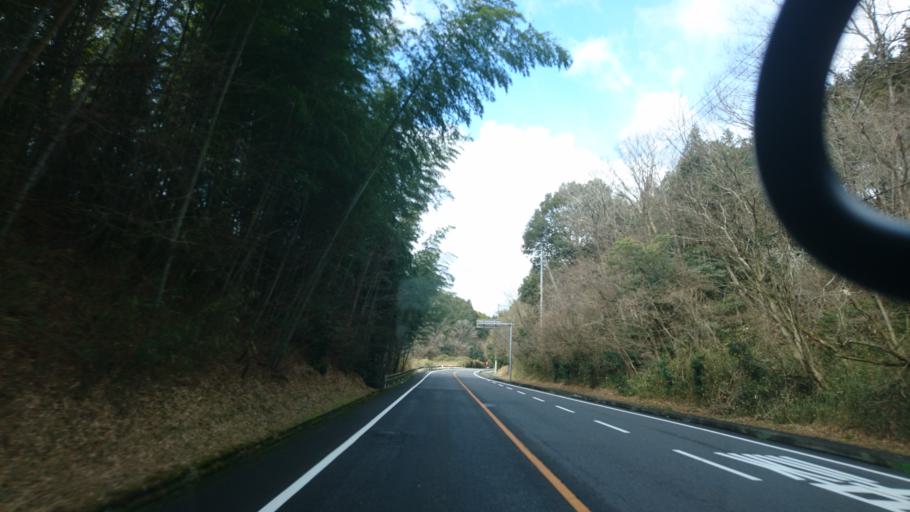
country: JP
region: Mie
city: Ueno-ebisumachi
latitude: 34.7582
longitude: 136.0668
